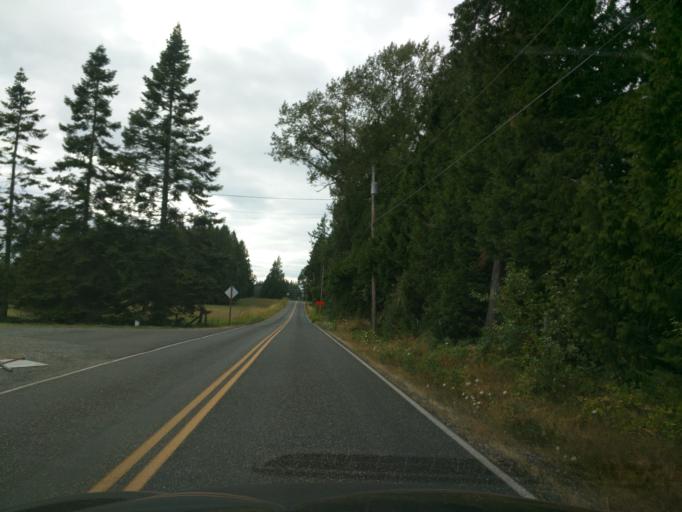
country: US
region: Washington
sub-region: Whatcom County
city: Bellingham
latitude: 48.8147
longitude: -122.4440
